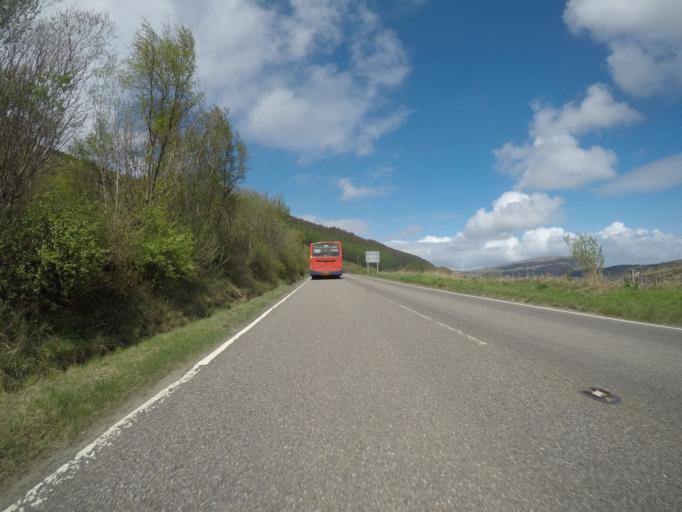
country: GB
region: Scotland
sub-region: Highland
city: Portree
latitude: 57.3888
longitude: -6.2046
